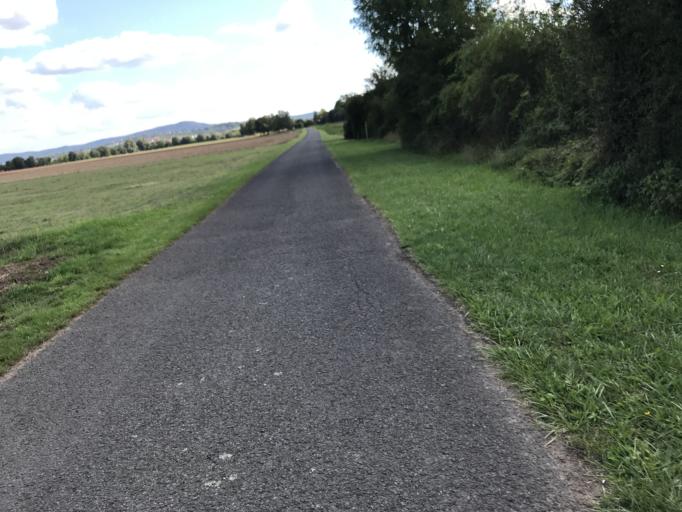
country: DE
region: Hesse
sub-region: Regierungsbezirk Kassel
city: Bad Sooden-Allendorf
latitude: 51.2147
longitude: 9.9964
